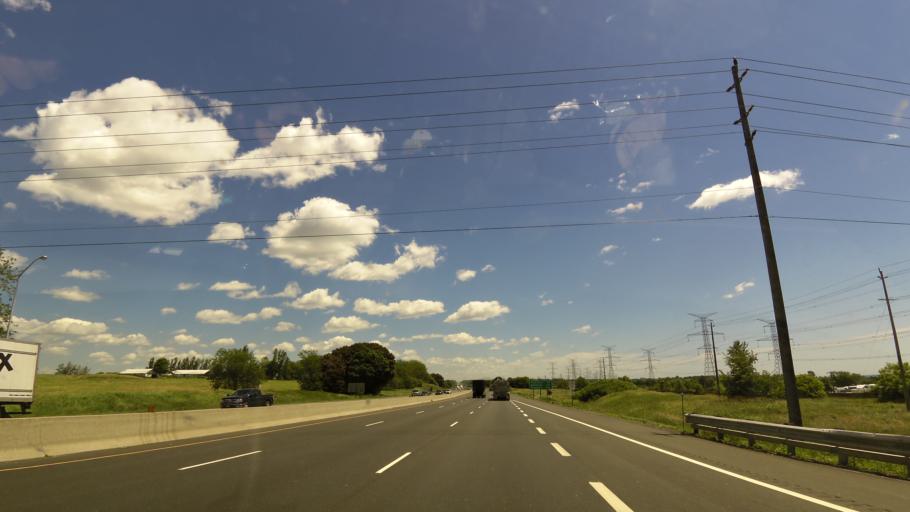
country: CA
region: Ontario
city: Oshawa
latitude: 43.9030
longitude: -78.6232
